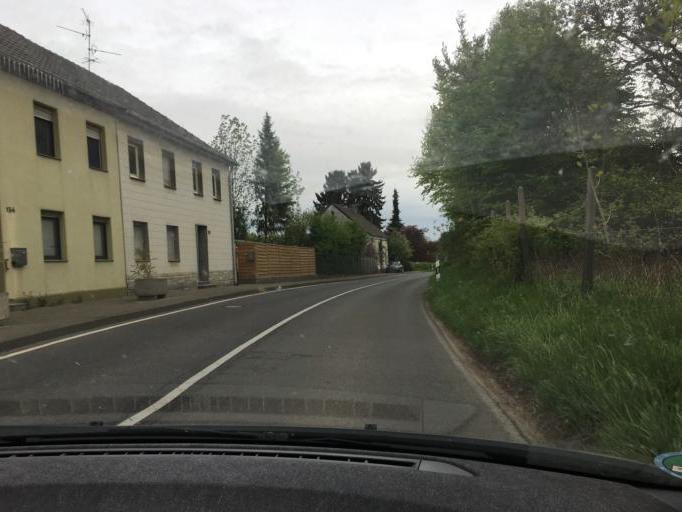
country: DE
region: North Rhine-Westphalia
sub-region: Regierungsbezirk Dusseldorf
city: Juchen
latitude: 51.1065
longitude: 6.4183
